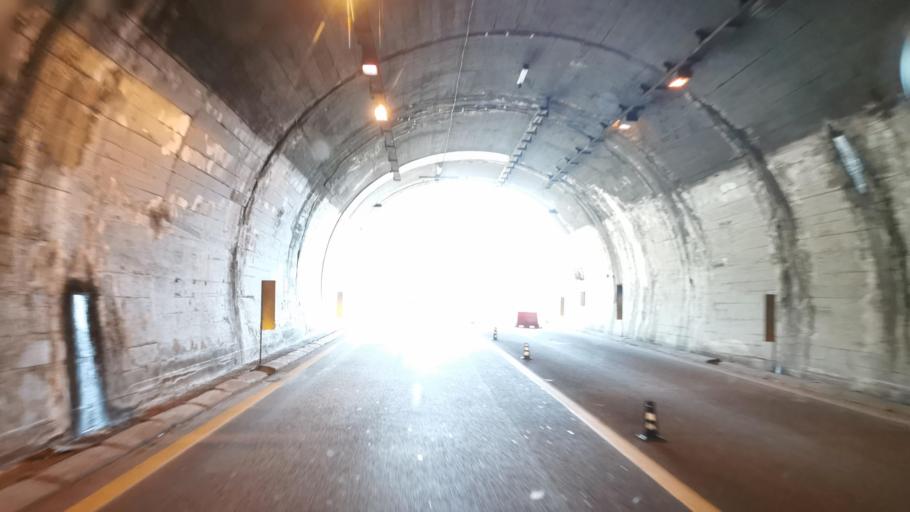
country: IT
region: Trentino-Alto Adige
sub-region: Provincia di Trento
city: Civezzano
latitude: 46.0825
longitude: 11.1768
